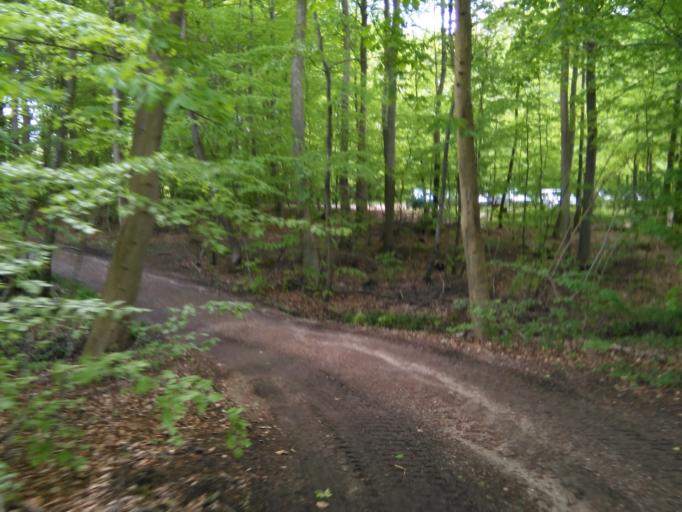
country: DK
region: Central Jutland
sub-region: Arhus Kommune
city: Beder
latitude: 56.0848
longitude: 10.2333
